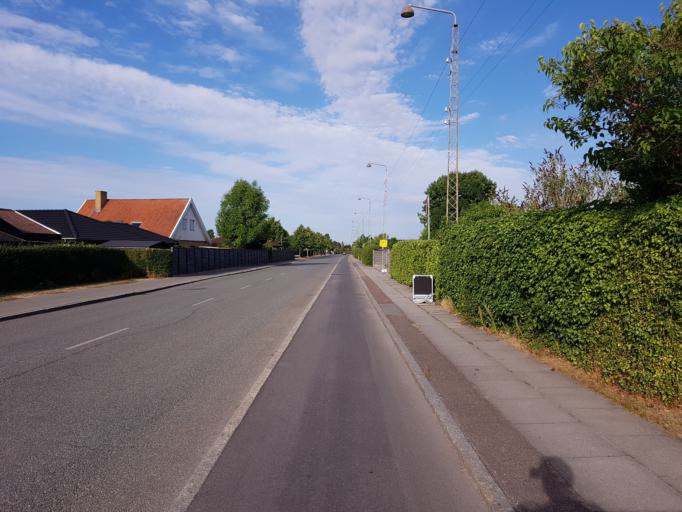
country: DK
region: Capital Region
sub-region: Tarnby Kommune
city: Tarnby
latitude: 55.6090
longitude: 12.5889
